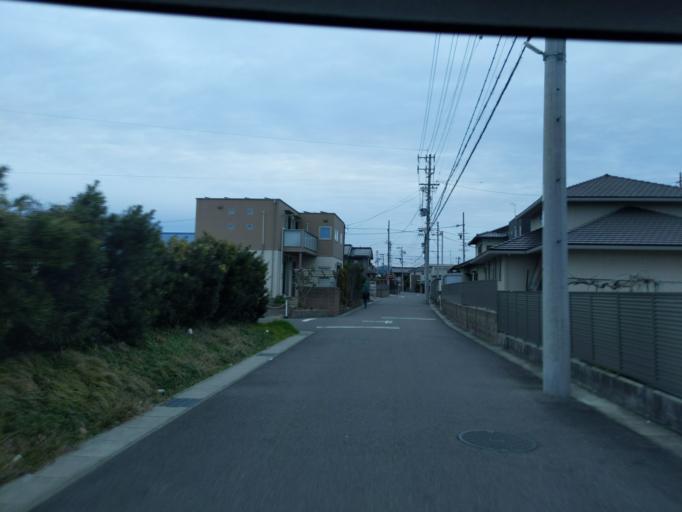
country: JP
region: Aichi
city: Kasugai
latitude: 35.2573
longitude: 136.9919
